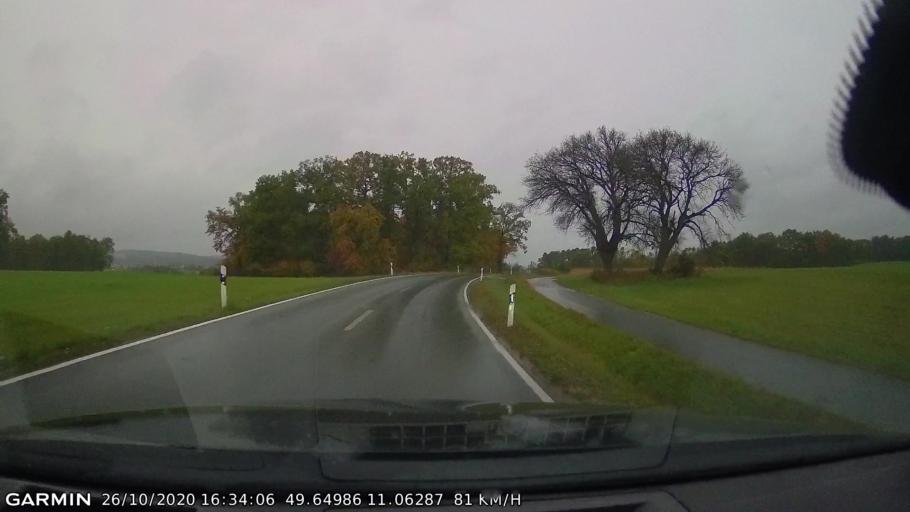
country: DE
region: Bavaria
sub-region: Upper Franconia
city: Langensendelbach
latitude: 49.6499
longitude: 11.0630
